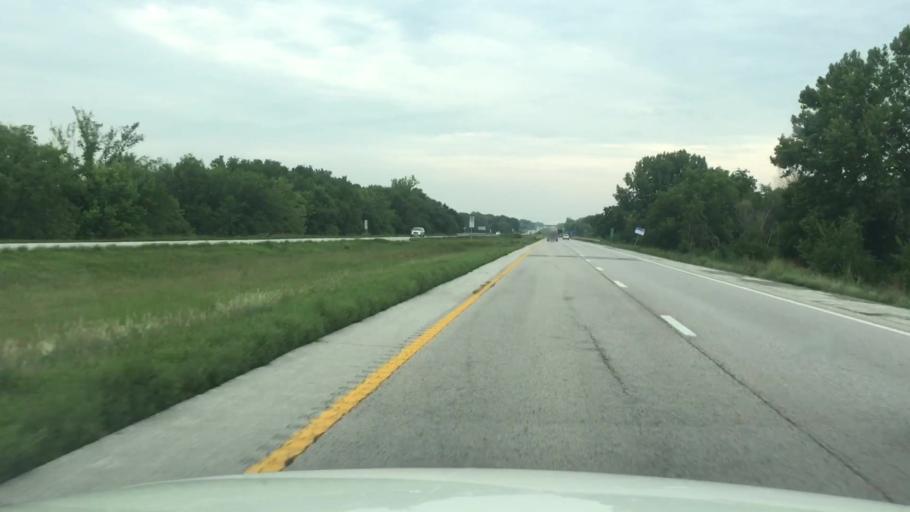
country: US
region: Missouri
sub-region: Clinton County
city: Cameron
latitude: 39.6830
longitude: -94.2320
